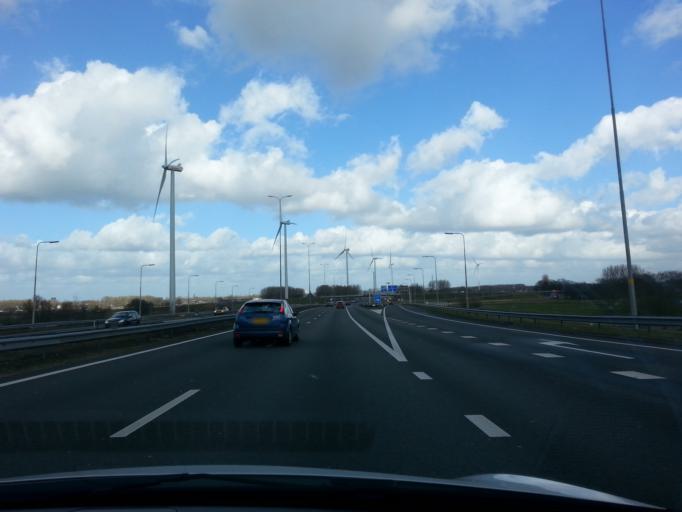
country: NL
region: Utrecht
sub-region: Gemeente Vianen
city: Vianen
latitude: 52.0073
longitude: 5.1170
